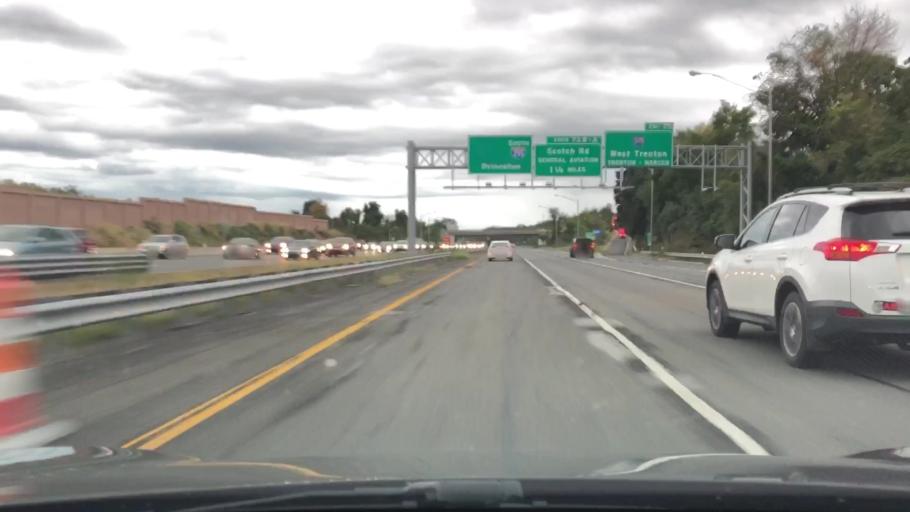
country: US
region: New Jersey
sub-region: Mercer County
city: Ewing
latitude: 40.2743
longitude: -74.8311
